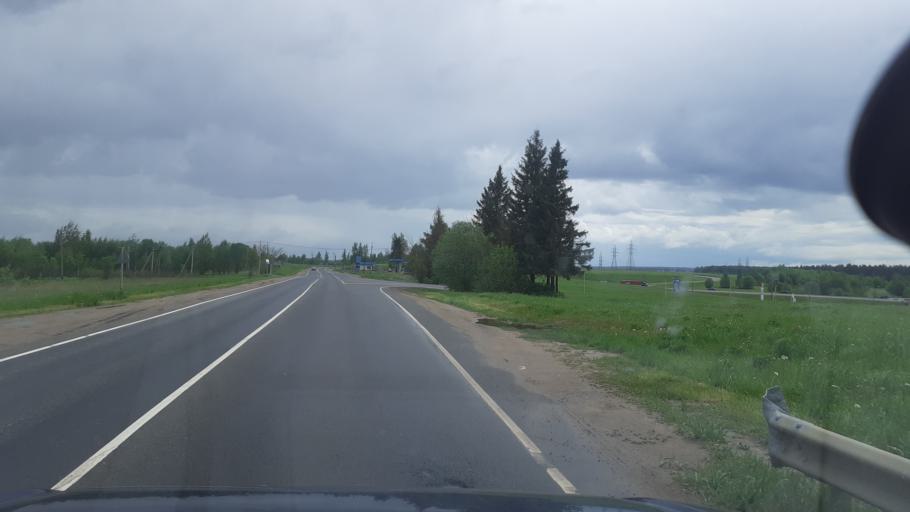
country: RU
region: Moskovskaya
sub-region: Volokolamskiy Rayon
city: Volokolamsk
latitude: 56.0252
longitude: 35.9644
